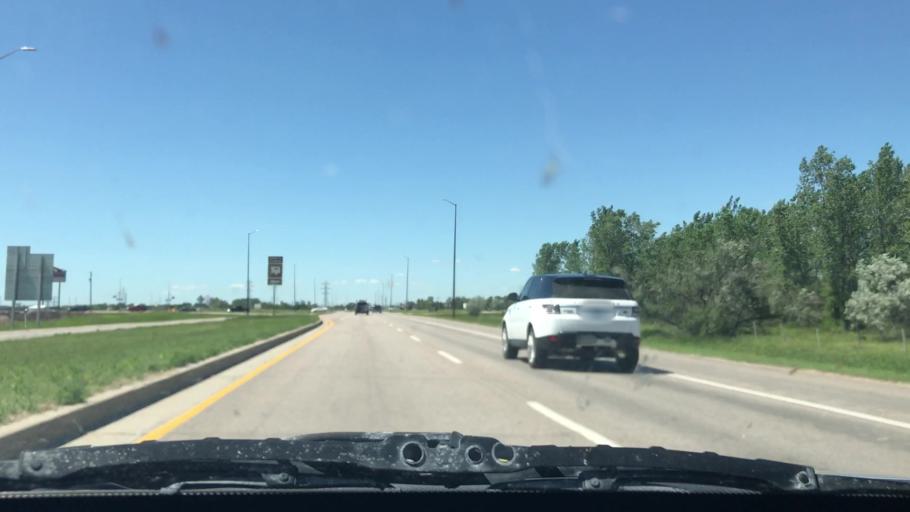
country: CA
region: Manitoba
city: Winnipeg
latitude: 49.8375
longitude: -96.9776
